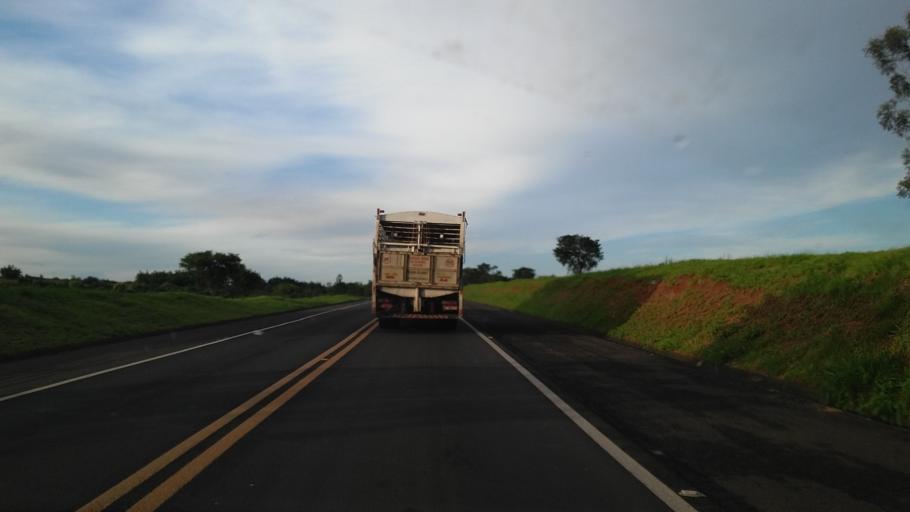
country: BR
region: Sao Paulo
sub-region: Marilia
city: Marilia
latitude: -21.9279
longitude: -49.9179
